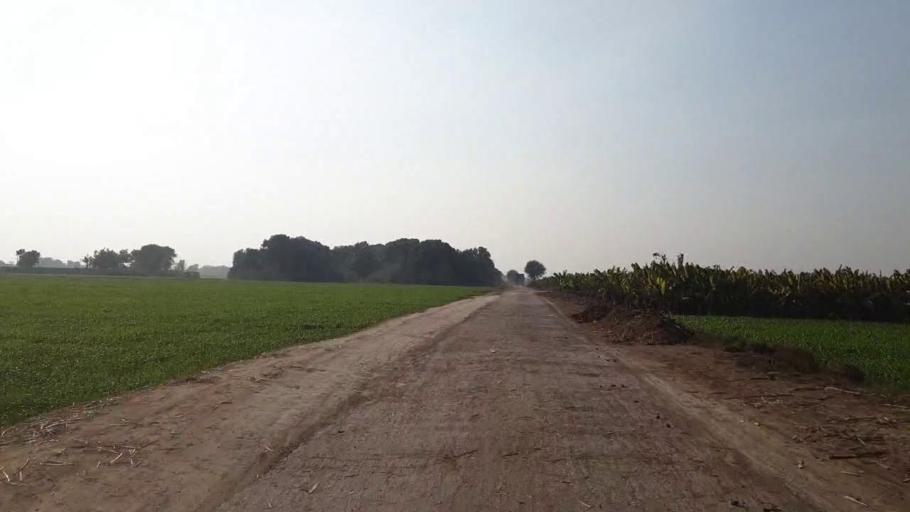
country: PK
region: Sindh
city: Matiari
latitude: 25.5995
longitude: 68.6122
